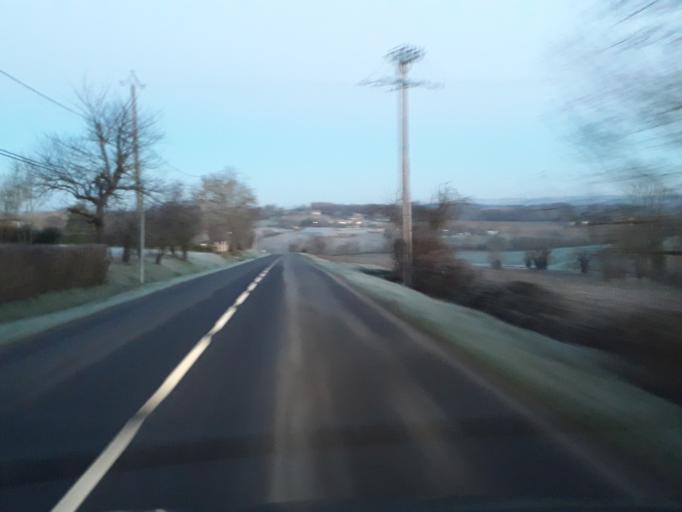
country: FR
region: Midi-Pyrenees
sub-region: Departement du Gers
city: Samatan
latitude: 43.4667
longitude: 0.9832
